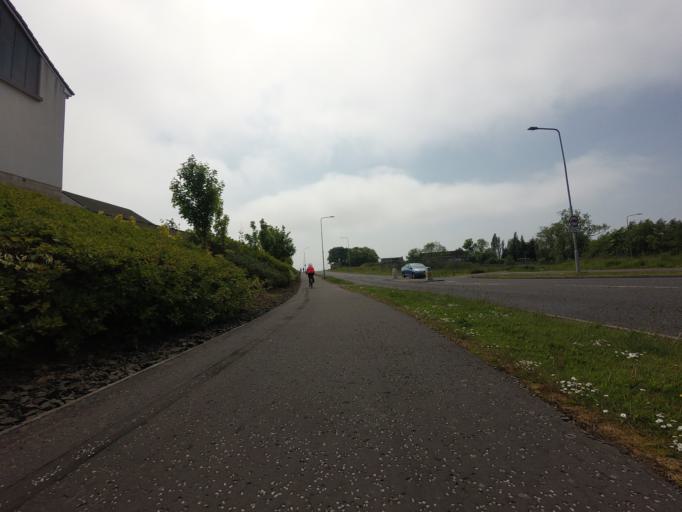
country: GB
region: Scotland
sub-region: Fife
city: Inverkeithing
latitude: 56.0509
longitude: -3.4114
